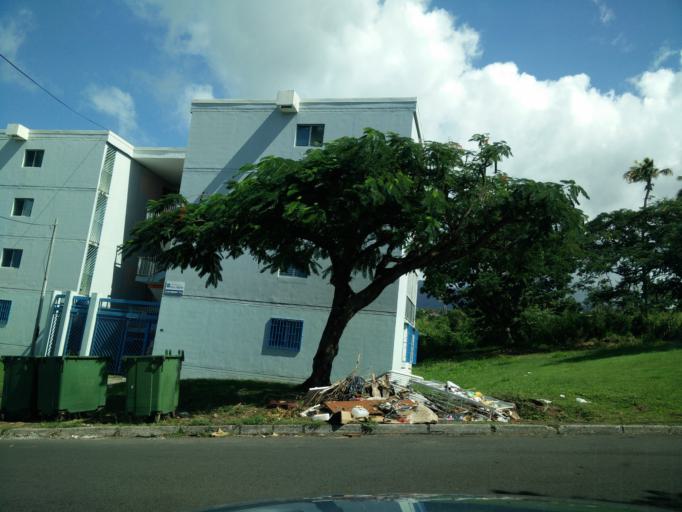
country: GP
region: Guadeloupe
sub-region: Guadeloupe
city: Basse-Terre
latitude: 15.9998
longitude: -61.7171
